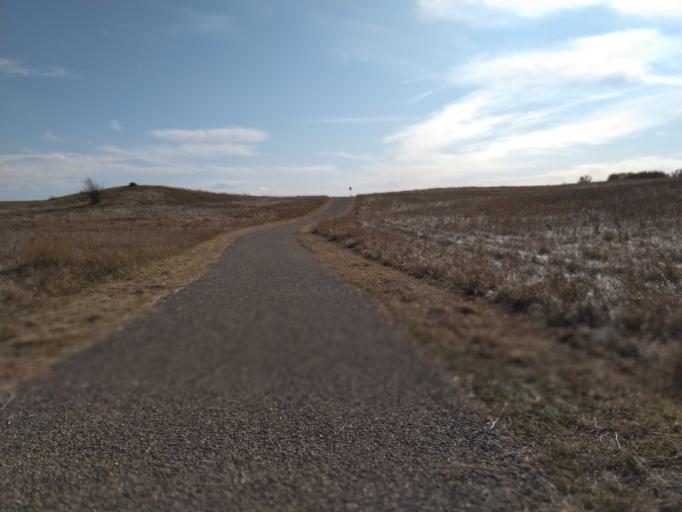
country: CA
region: Alberta
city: Calgary
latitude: 51.1235
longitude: -114.1265
